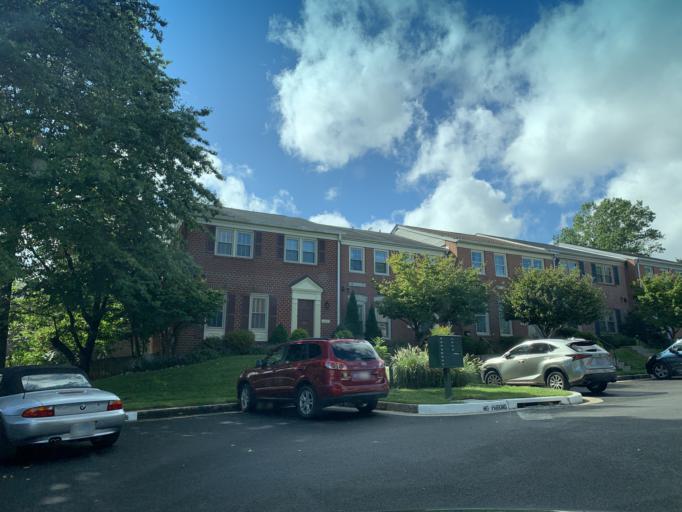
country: US
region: Maryland
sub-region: Baltimore County
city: Timonium
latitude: 39.4478
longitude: -76.6124
